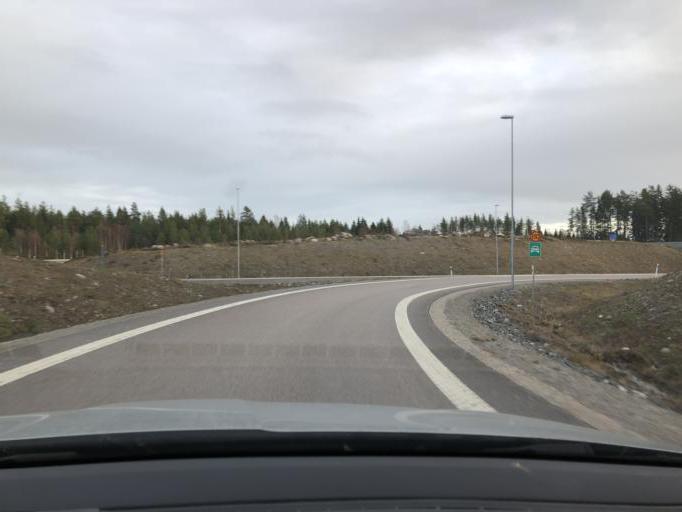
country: SE
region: Gaevleborg
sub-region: Hudiksvalls Kommun
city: Iggesund
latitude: 61.5528
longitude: 16.9746
